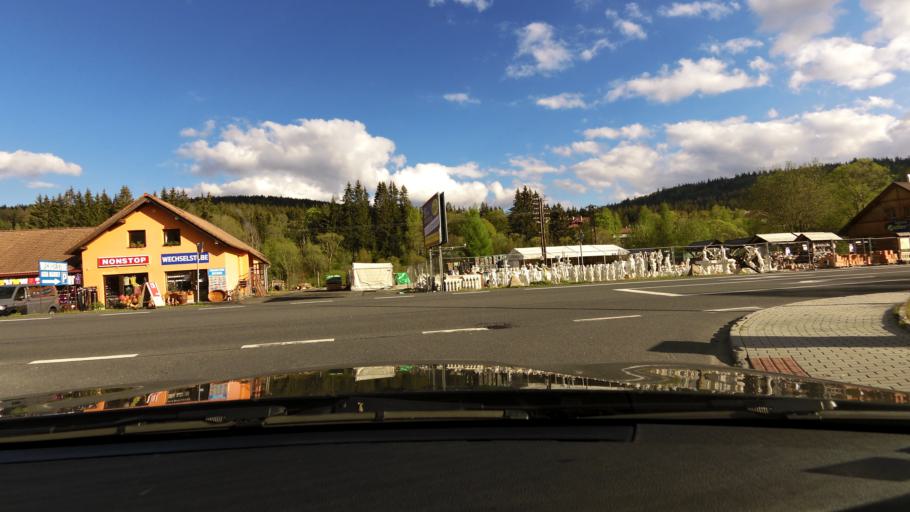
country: DE
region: Bavaria
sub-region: Lower Bavaria
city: Bayerisch Eisenstein
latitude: 49.1243
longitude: 13.2093
